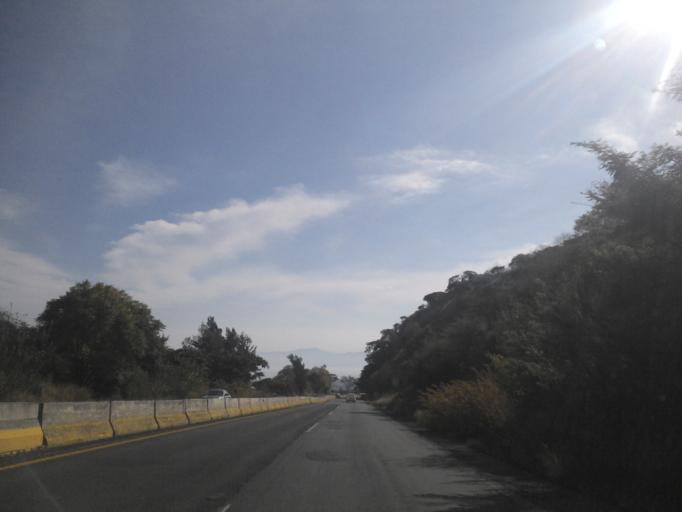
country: MX
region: Jalisco
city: Ixtlahuacan de los Membrillos
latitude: 20.3312
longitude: -103.1834
